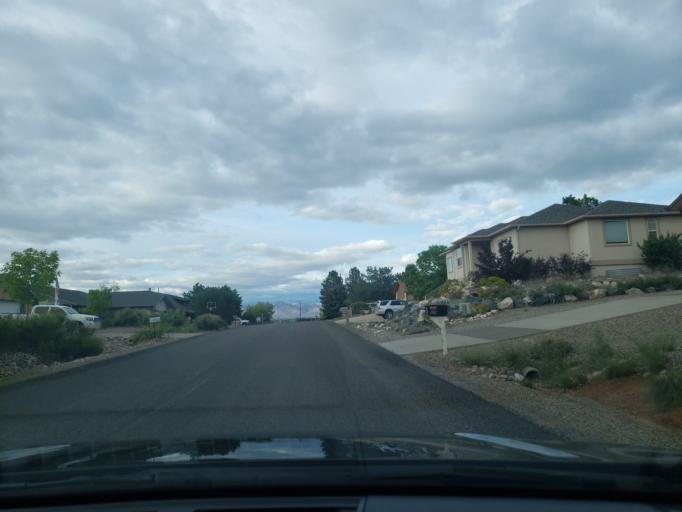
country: US
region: Colorado
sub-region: Mesa County
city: Fruita
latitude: 39.1374
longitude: -108.7437
